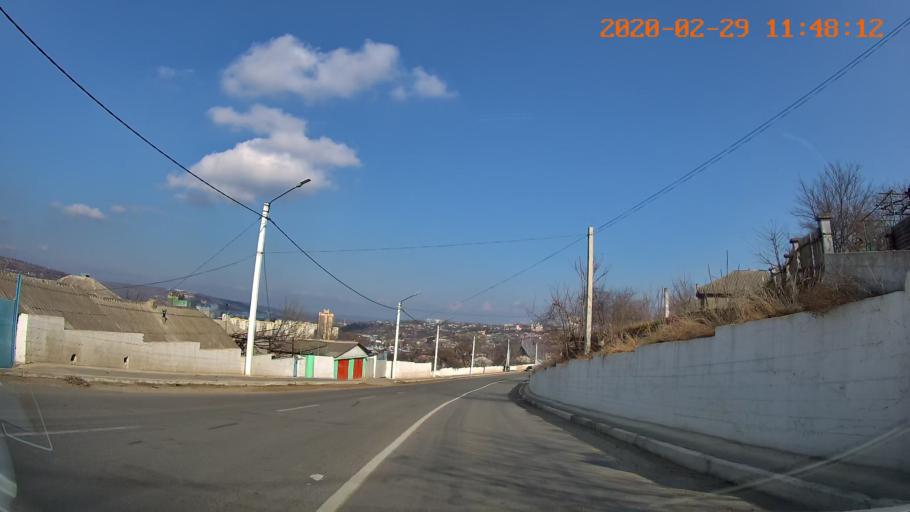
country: MD
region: Rezina
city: Rezina
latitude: 47.7468
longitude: 28.9892
